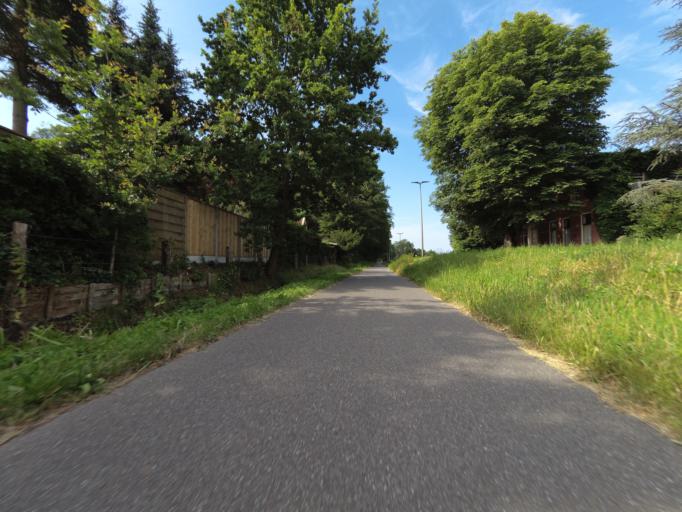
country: NL
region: Overijssel
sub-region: Gemeente Enschede
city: Enschede
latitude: 52.2460
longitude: 6.9081
